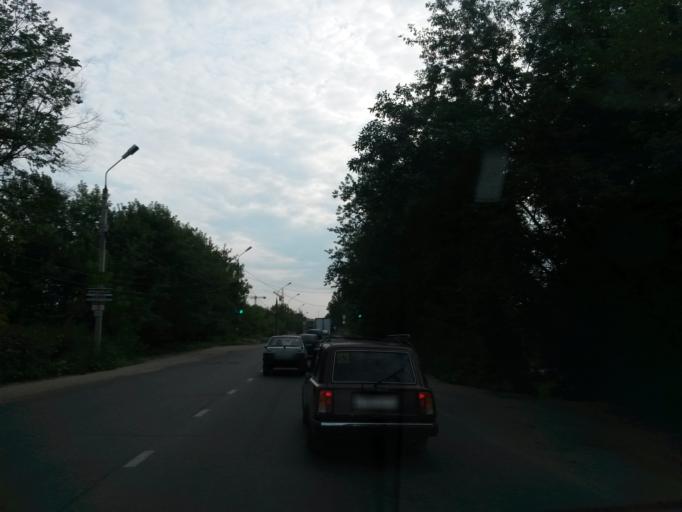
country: RU
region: Jaroslavl
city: Yaroslavl
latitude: 57.6112
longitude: 39.8386
